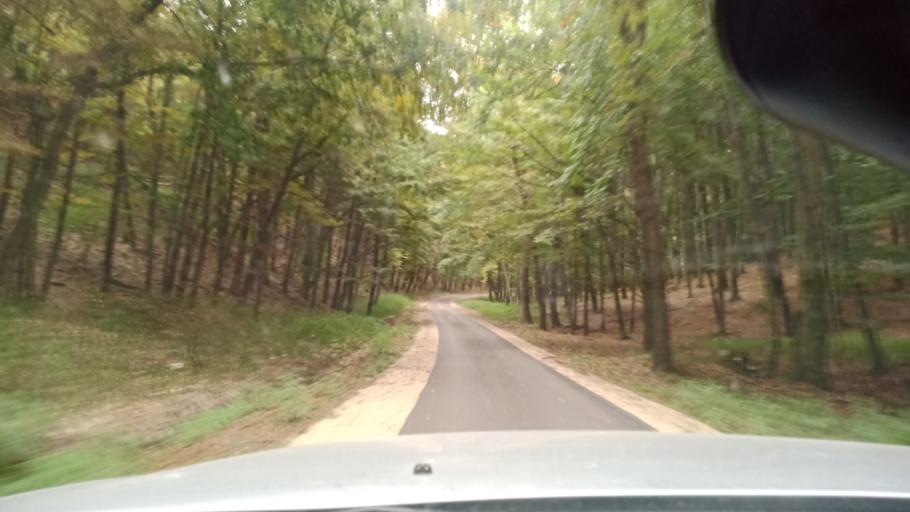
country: HU
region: Komarom-Esztergom
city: Oroszlany
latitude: 47.3868
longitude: 18.3232
